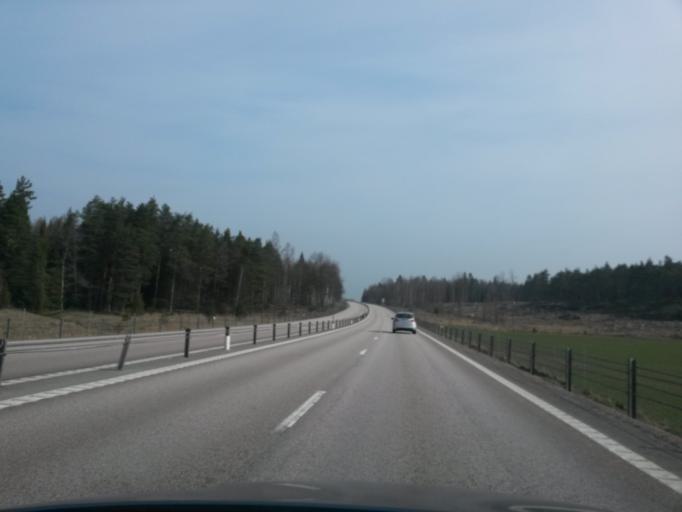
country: SE
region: Vaestra Goetaland
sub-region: Toreboda Kommun
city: Toereboda
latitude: 58.7670
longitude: 13.9850
